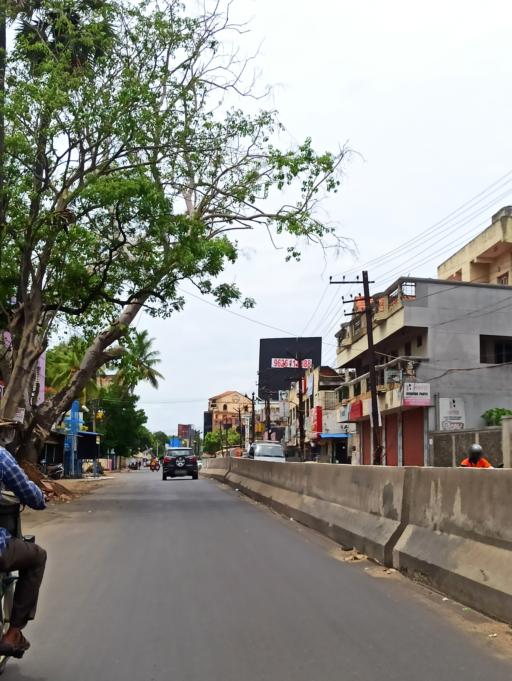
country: IN
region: Tamil Nadu
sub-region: Kancheepuram
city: Vandalur
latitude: 12.9230
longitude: 80.0967
